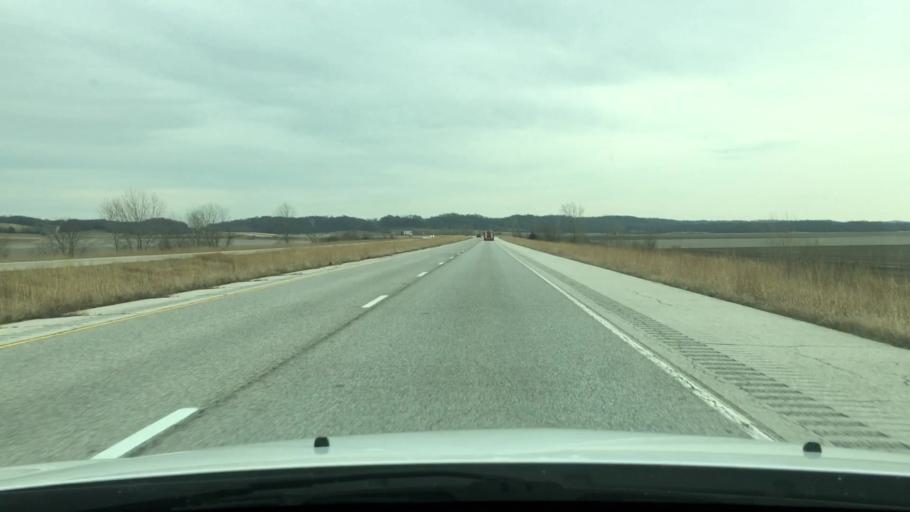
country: US
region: Illinois
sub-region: Pike County
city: Griggsville
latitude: 39.6879
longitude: -90.5962
